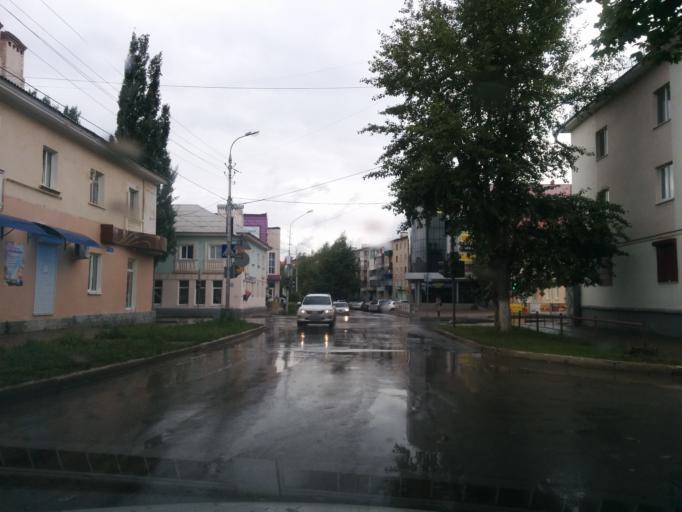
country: RU
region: Bashkortostan
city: Oktyabr'skiy
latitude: 54.4835
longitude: 53.4800
